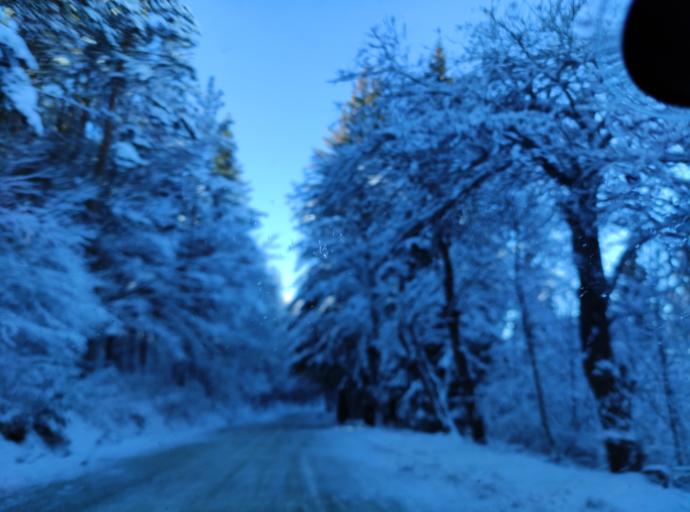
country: BG
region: Sofia-Capital
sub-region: Stolichna Obshtina
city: Sofia
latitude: 42.5953
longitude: 23.3098
